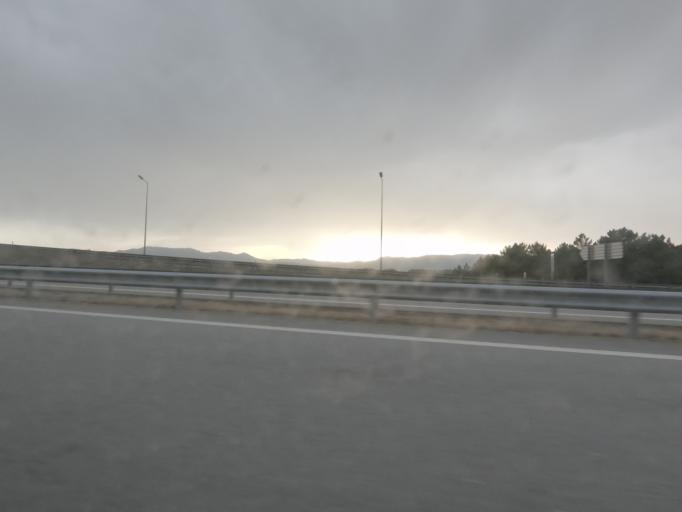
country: PT
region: Vila Real
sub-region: Vila Real
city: Vila Real
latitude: 41.2571
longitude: -7.7127
